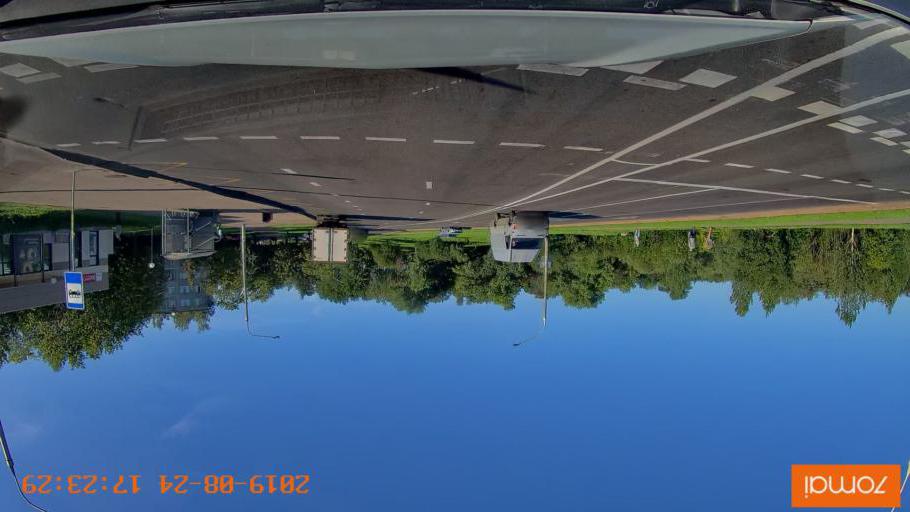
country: BY
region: Minsk
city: Hatava
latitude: 53.8425
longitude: 27.6510
